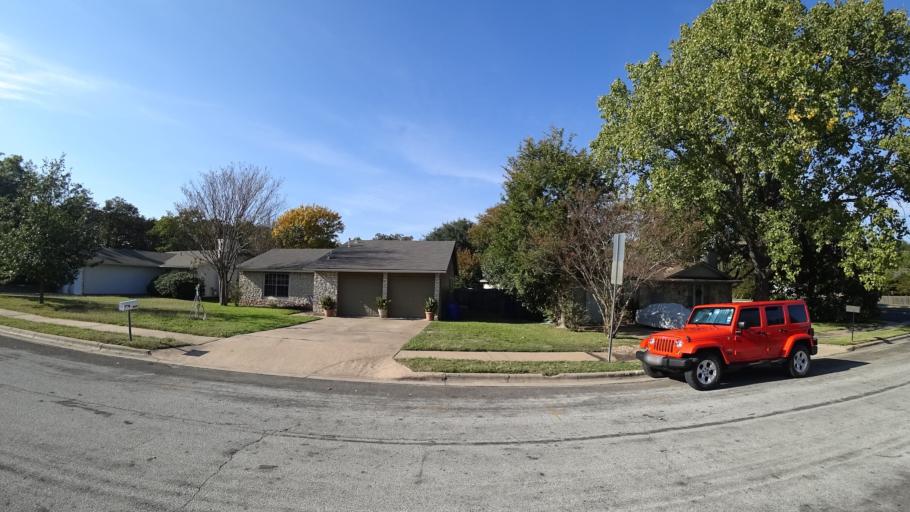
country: US
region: Texas
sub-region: Williamson County
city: Anderson Mill
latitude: 30.4588
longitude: -97.8145
